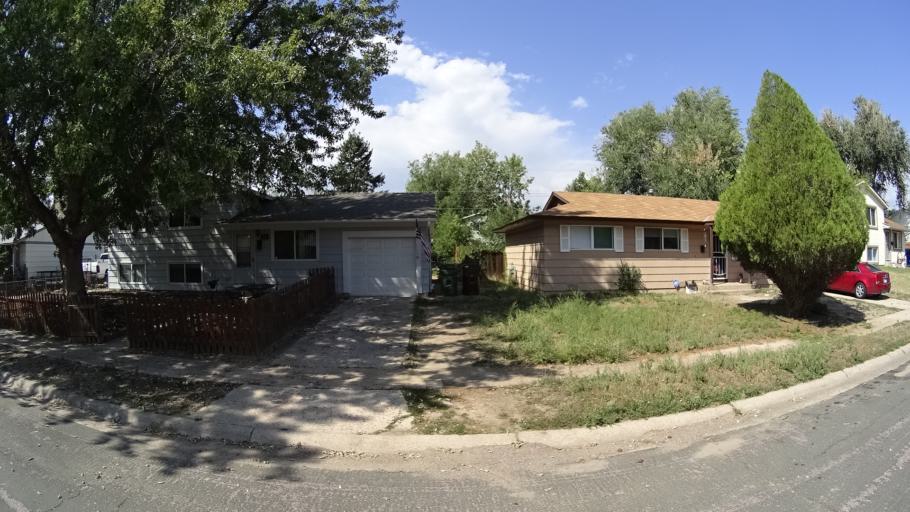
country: US
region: Colorado
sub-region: El Paso County
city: Colorado Springs
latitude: 38.8202
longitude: -104.7826
